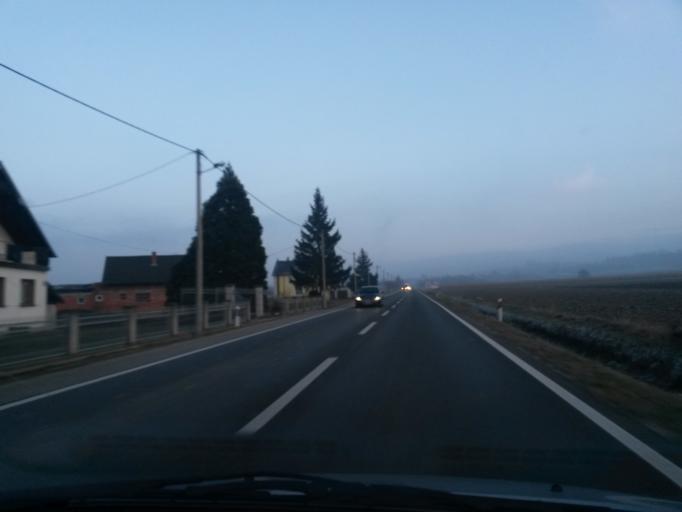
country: HR
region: Koprivnicko-Krizevacka
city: Reka
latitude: 46.1953
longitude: 16.7249
